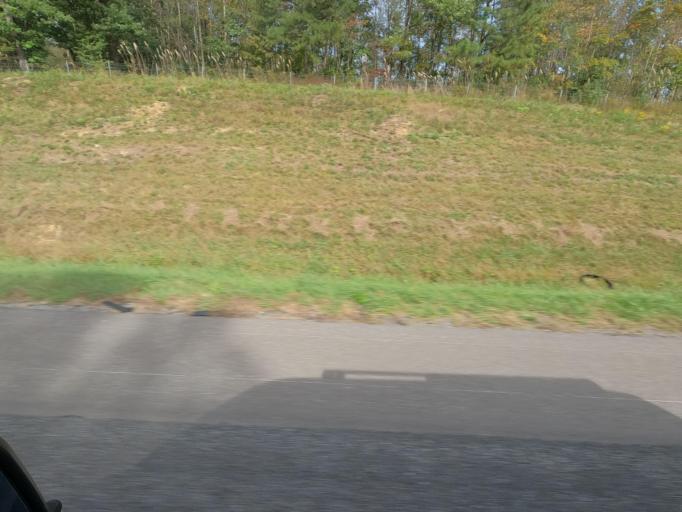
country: US
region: Tennessee
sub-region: Decatur County
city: Parsons
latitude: 35.8173
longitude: -88.2353
